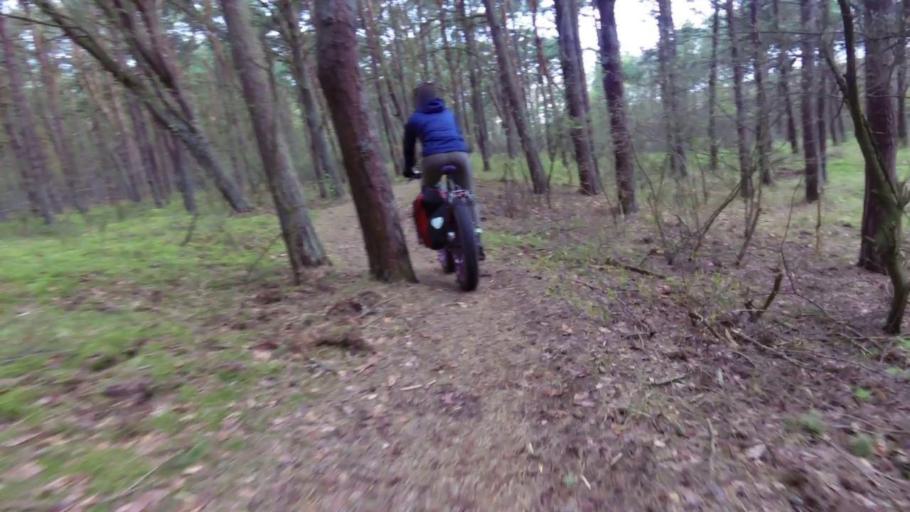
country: PL
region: West Pomeranian Voivodeship
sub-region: Powiat kamienski
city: Dziwnow
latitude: 53.9998
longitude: 14.6579
